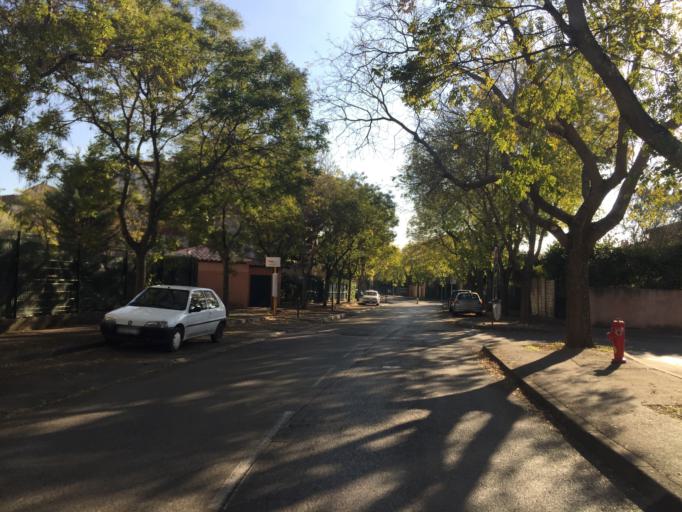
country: FR
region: Provence-Alpes-Cote d'Azur
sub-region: Departement des Bouches-du-Rhone
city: Aix-en-Provence
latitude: 43.5297
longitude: 5.4105
